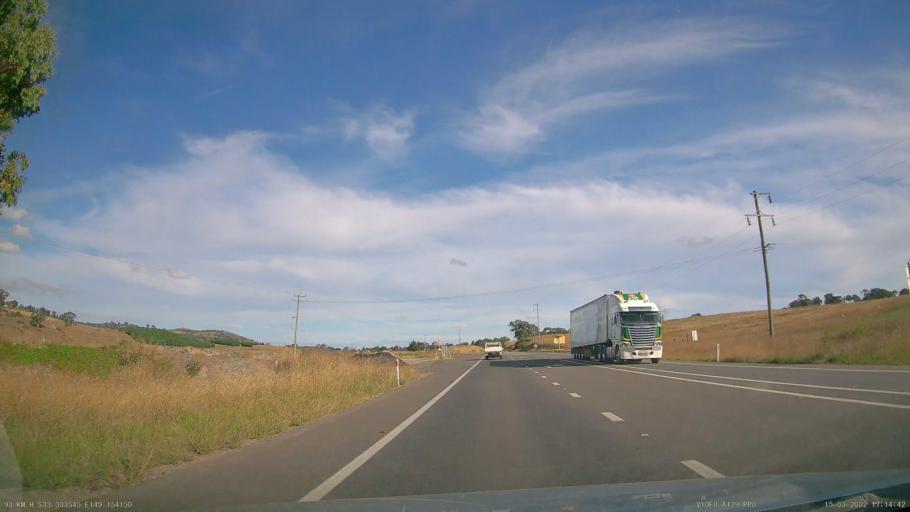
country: AU
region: New South Wales
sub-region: Orange Municipality
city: Orange
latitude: -33.3337
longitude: 149.1542
